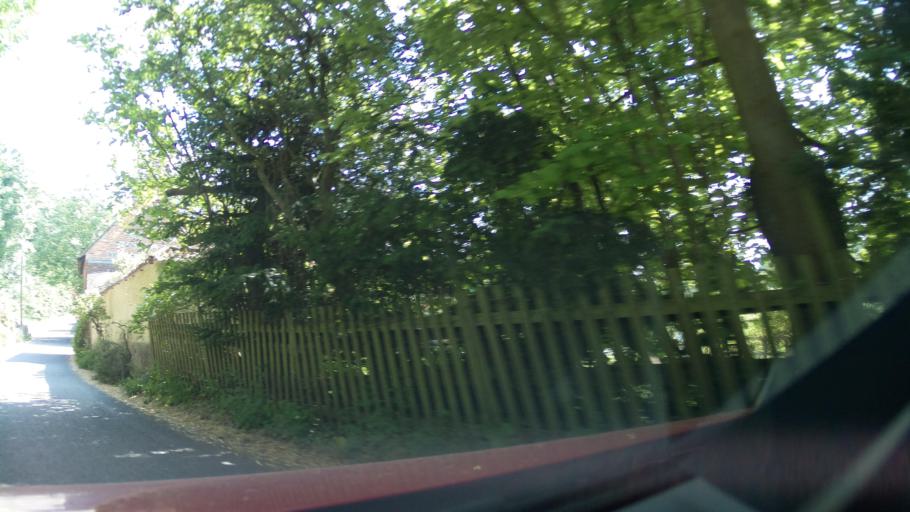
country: GB
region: England
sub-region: Wiltshire
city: Rushall
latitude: 51.2656
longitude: -1.7971
